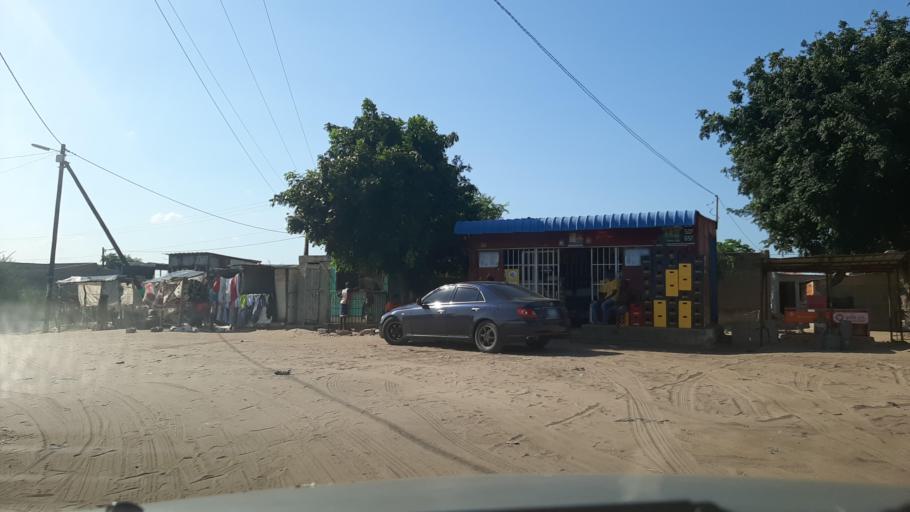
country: MZ
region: Maputo
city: Matola
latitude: -25.7903
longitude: 32.4879
